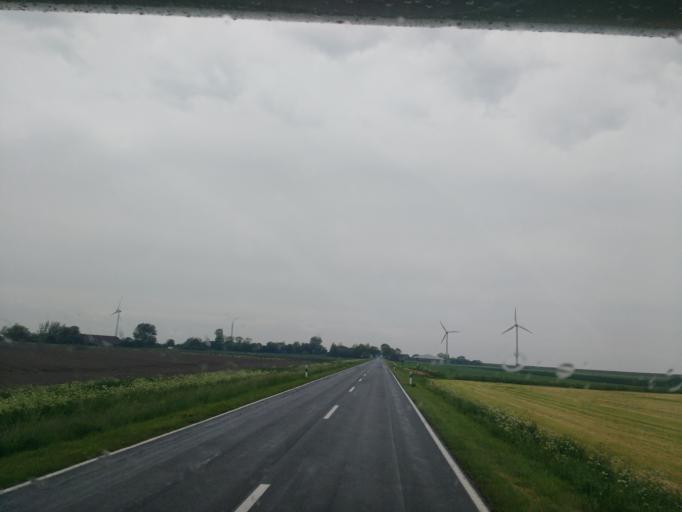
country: DE
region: Lower Saxony
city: Werdum
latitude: 53.6924
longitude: 7.7660
